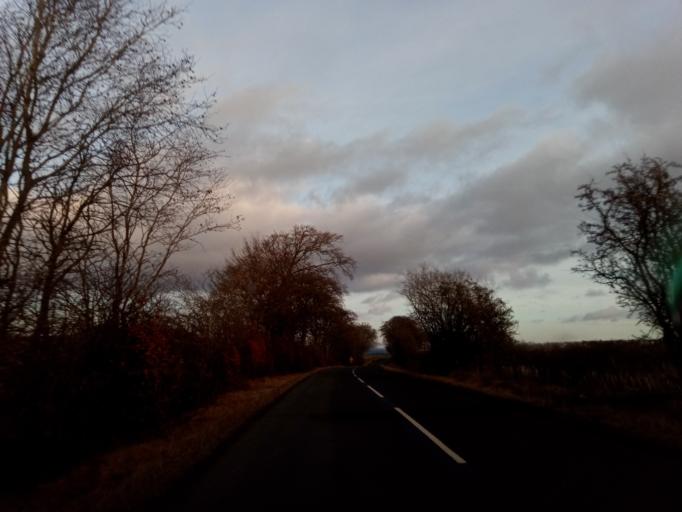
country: GB
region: Scotland
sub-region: The Scottish Borders
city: Melrose
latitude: 55.5511
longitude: -2.7665
